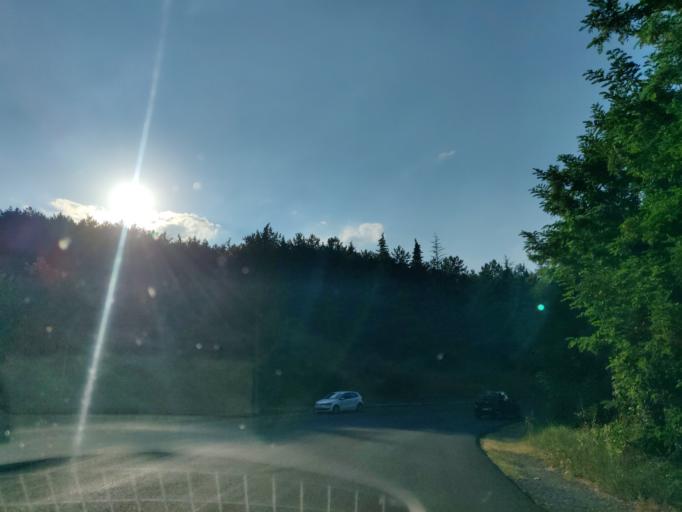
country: IT
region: Tuscany
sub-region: Provincia di Siena
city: Abbadia San Salvatore
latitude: 42.8720
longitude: 11.6842
